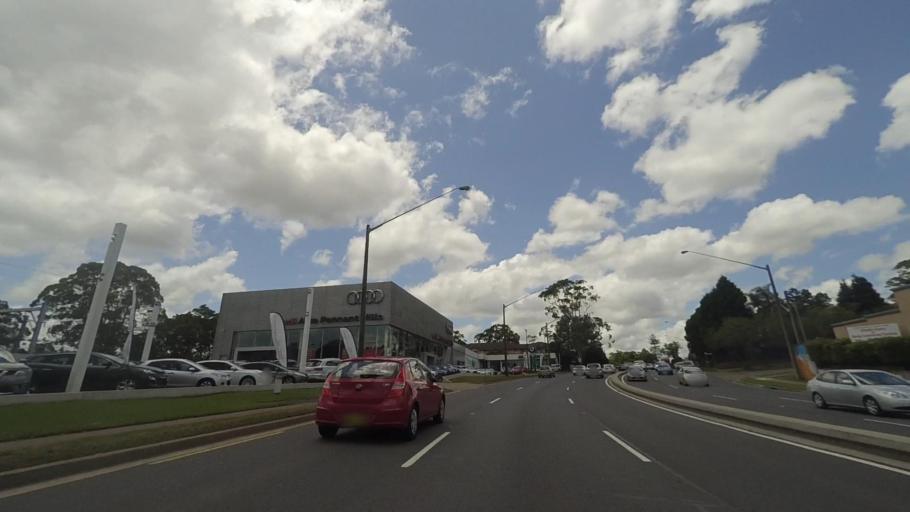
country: AU
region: New South Wales
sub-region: Hornsby Shire
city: Pennant Hills
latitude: -33.7367
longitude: 151.0747
